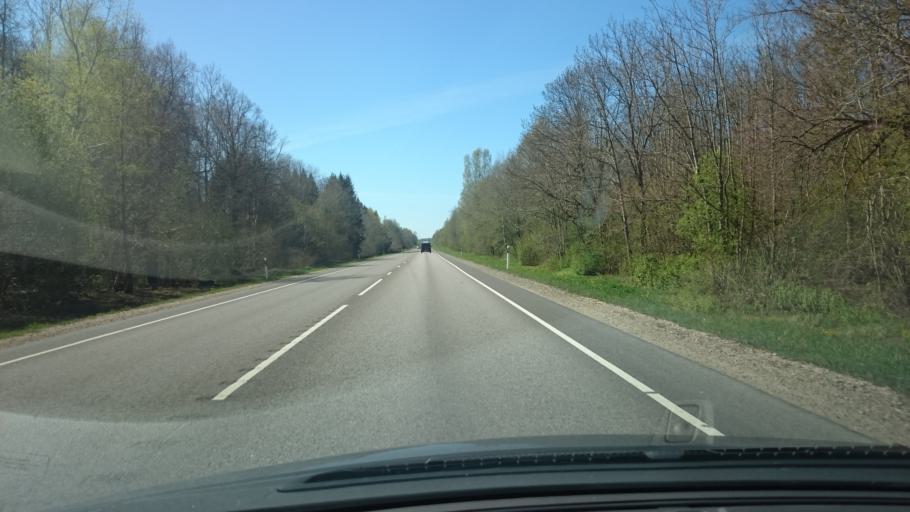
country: EE
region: Ida-Virumaa
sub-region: Sillamaee linn
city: Sillamae
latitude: 59.3812
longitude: 27.8547
